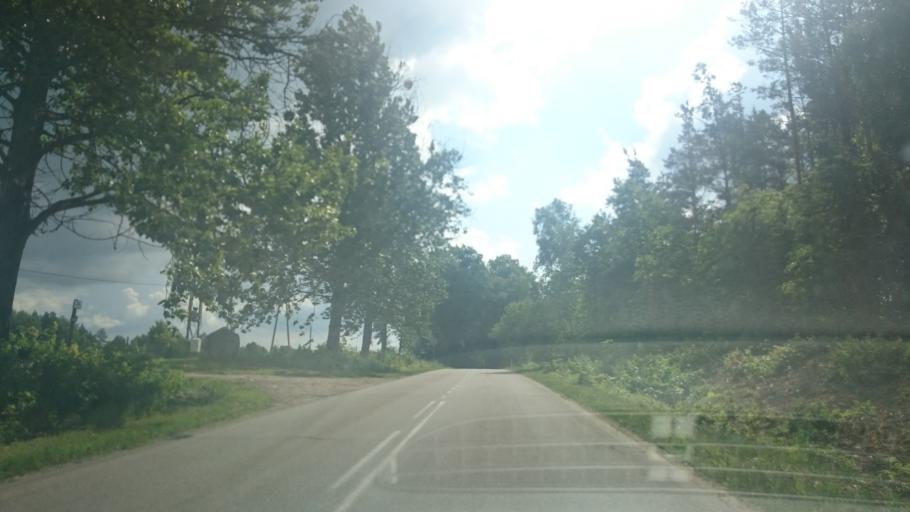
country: PL
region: Pomeranian Voivodeship
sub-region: Powiat starogardzki
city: Kaliska
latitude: 53.9683
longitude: 18.2491
